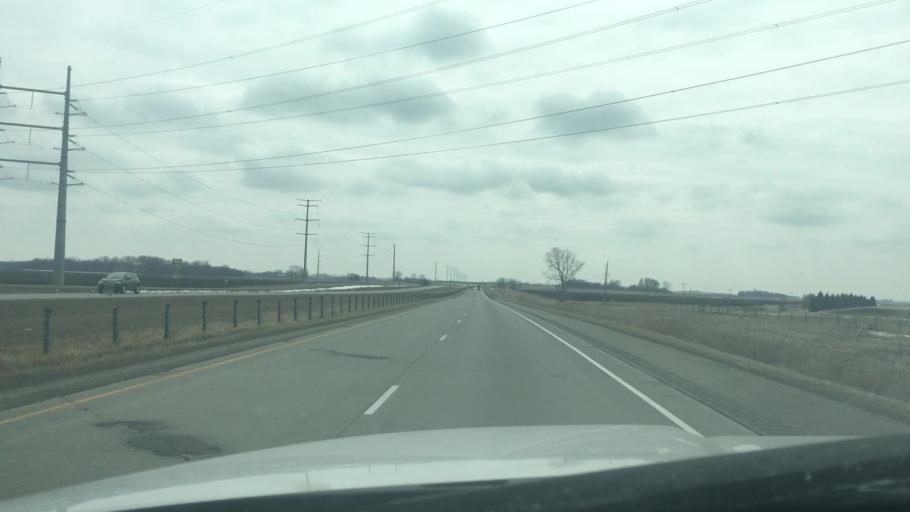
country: US
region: Minnesota
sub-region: Clay County
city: Barnesville
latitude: 46.5696
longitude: -96.3239
